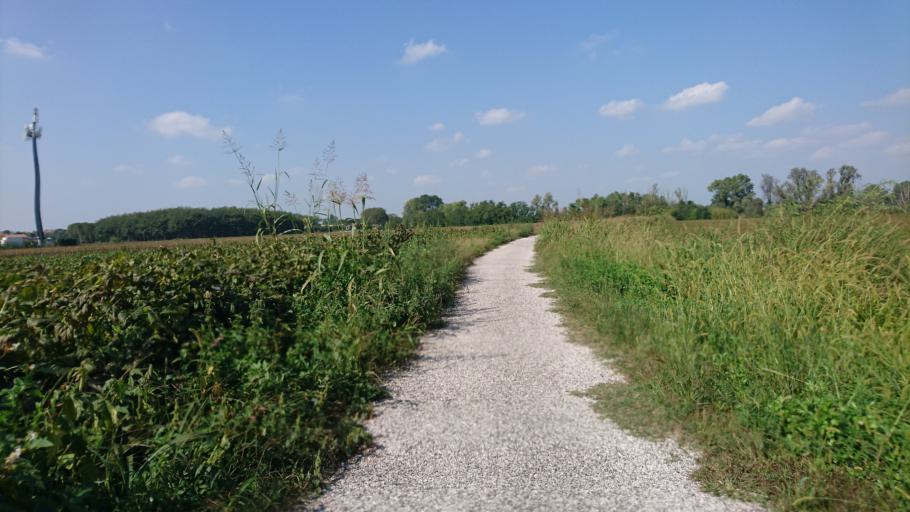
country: IT
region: Veneto
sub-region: Provincia di Padova
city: Piazzola sul Brenta
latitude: 45.5434
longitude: 11.8006
